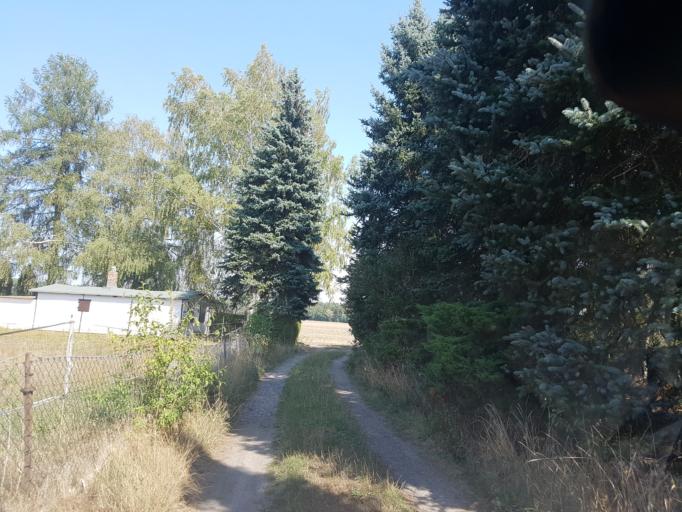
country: DE
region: Brandenburg
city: Wiesenburg
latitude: 52.0699
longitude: 12.3865
